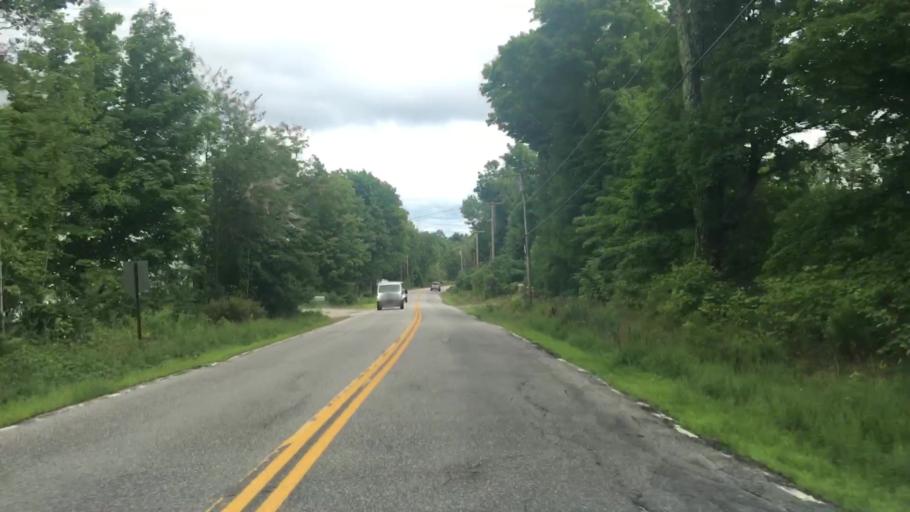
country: US
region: Maine
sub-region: York County
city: Limerick
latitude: 43.6778
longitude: -70.7855
